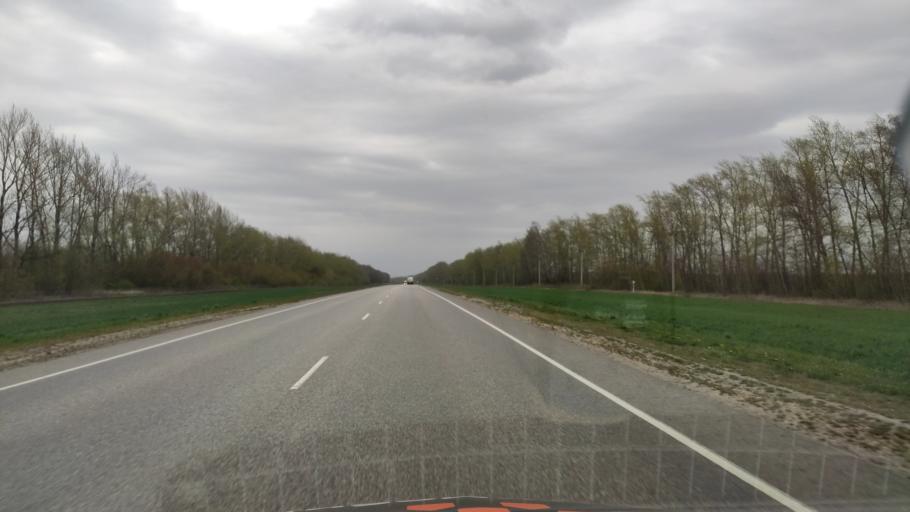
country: RU
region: Kursk
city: Olym
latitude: 51.5498
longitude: 38.1703
